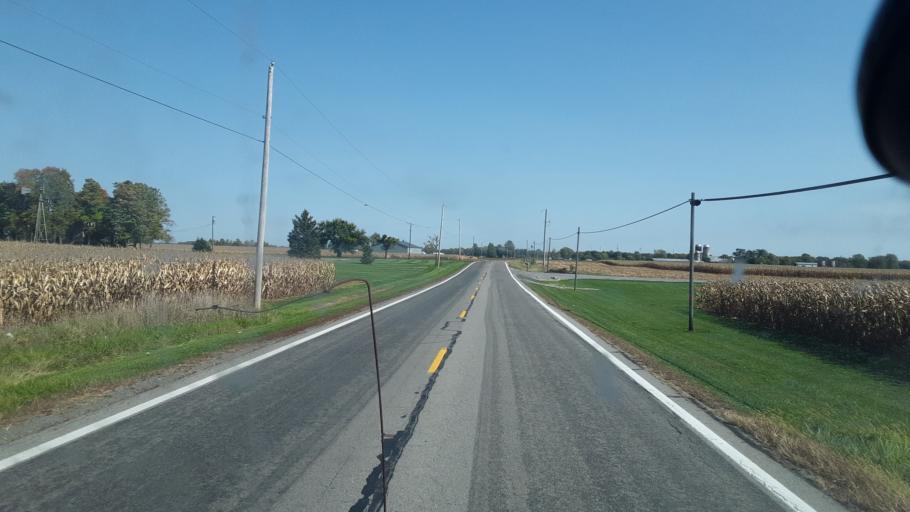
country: US
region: Ohio
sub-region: Logan County
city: Northwood
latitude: 40.5106
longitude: -83.7744
